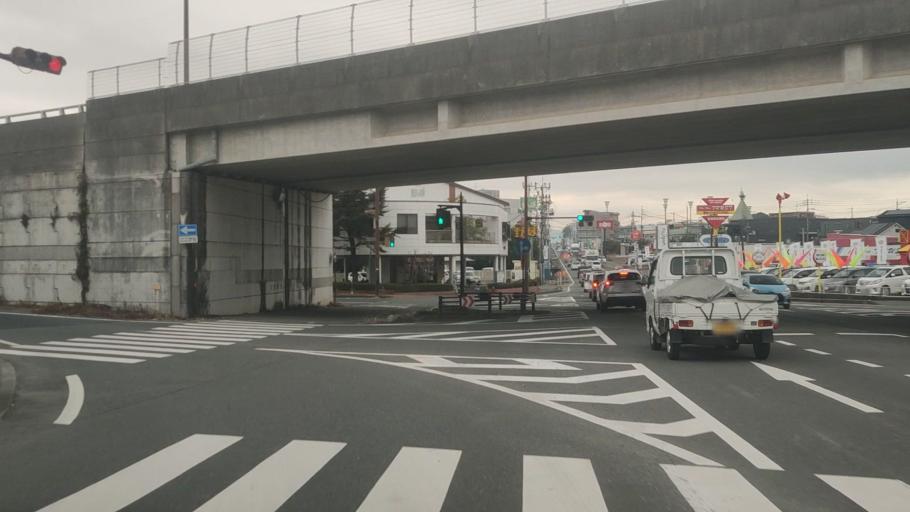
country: JP
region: Kumamoto
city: Ozu
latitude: 32.8258
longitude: 130.7922
